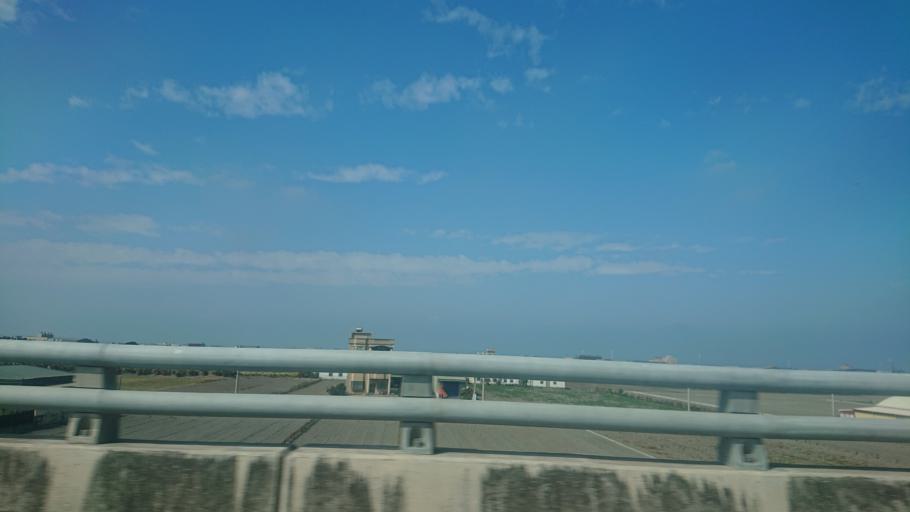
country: TW
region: Taiwan
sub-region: Changhua
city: Chang-hua
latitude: 24.0449
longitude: 120.4067
